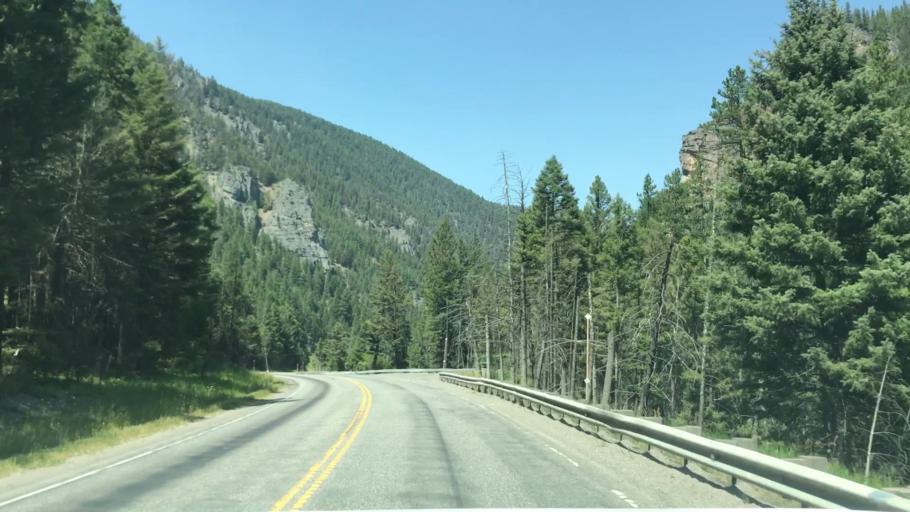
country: US
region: Montana
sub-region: Gallatin County
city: Big Sky
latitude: 45.4124
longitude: -111.2287
